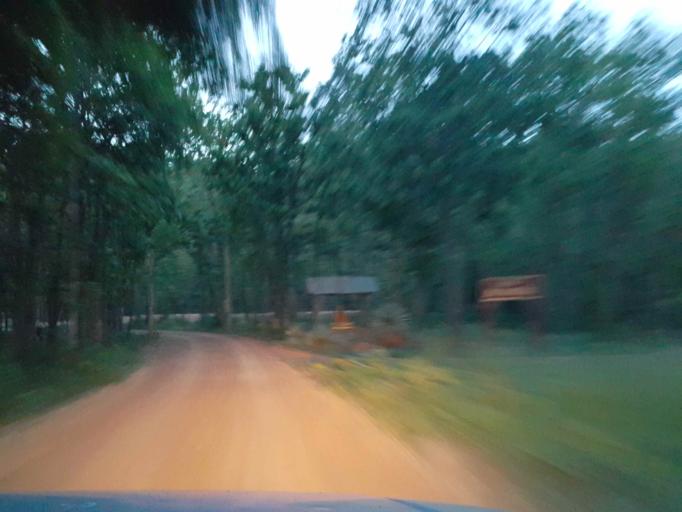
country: TH
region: Sukhothai
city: Thung Saliam
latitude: 17.2203
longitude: 99.5414
